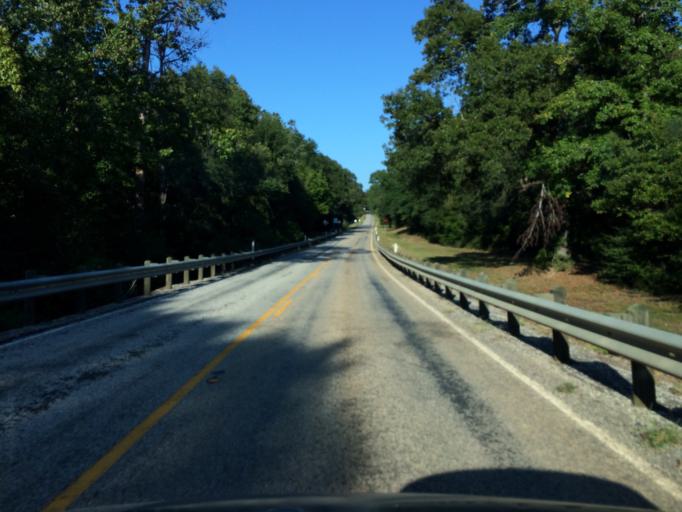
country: US
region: Texas
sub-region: Wood County
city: Hawkins
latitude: 32.6381
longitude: -95.2589
